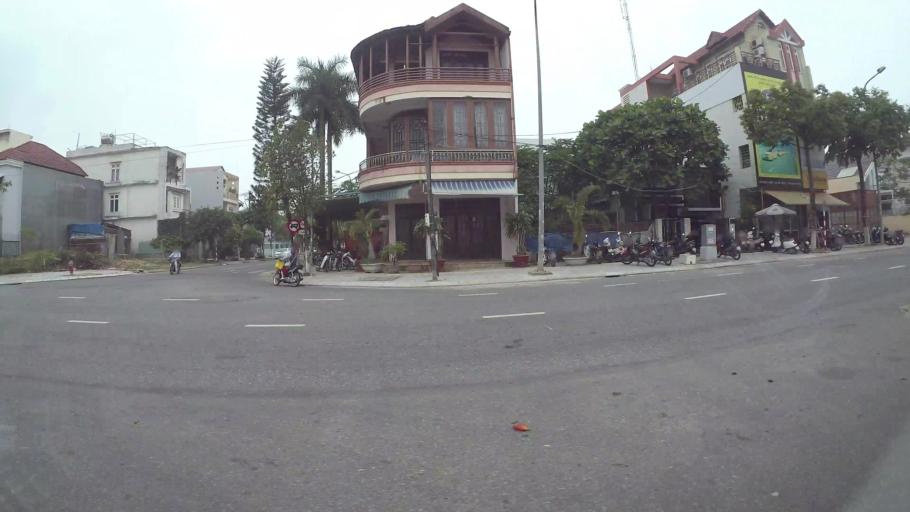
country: VN
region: Da Nang
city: Cam Le
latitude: 16.0254
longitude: 108.2153
